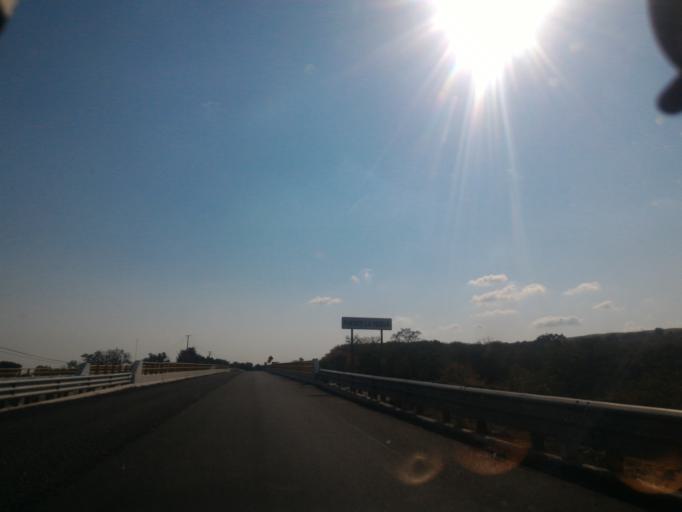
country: MX
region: Jalisco
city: Tonila
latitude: 19.4161
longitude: -103.5210
